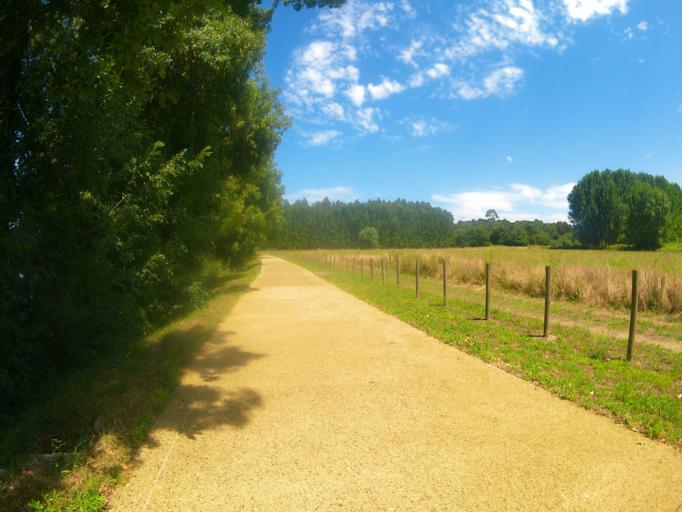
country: ES
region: Galicia
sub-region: Provincia de Pontevedra
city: Tomino
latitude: 41.9842
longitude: -8.6941
